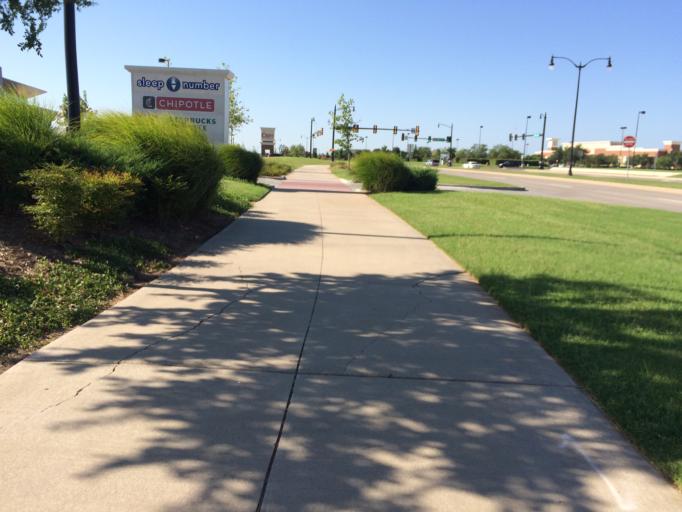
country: US
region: Oklahoma
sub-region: Cleveland County
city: Norman
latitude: 35.2384
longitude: -97.4820
